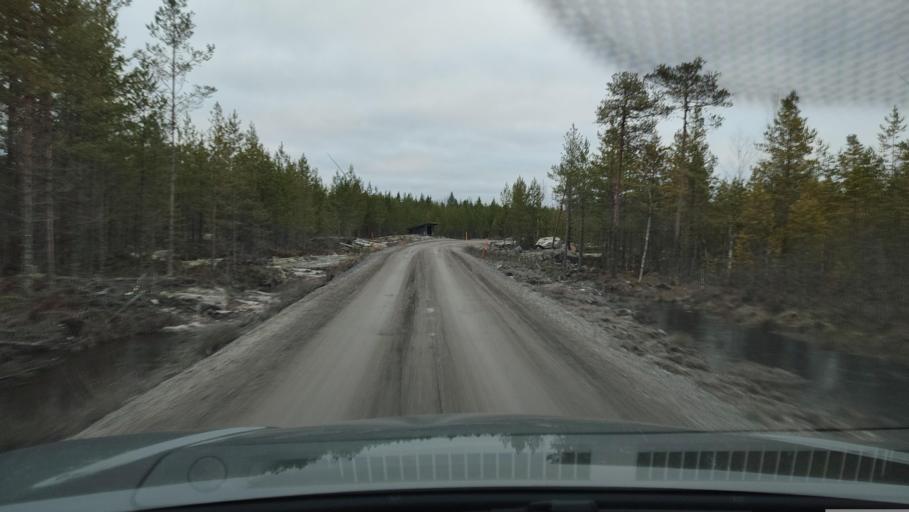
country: FI
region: Southern Ostrobothnia
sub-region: Suupohja
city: Karijoki
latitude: 62.1898
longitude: 21.5679
